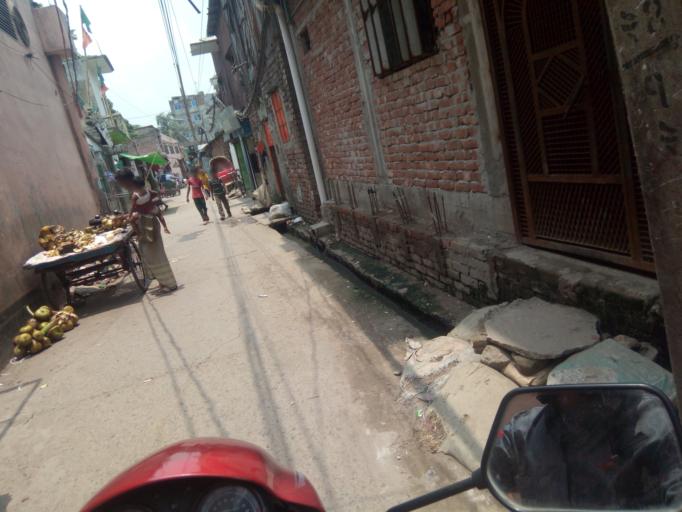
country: BD
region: Dhaka
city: Azimpur
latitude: 23.7175
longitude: 90.3799
